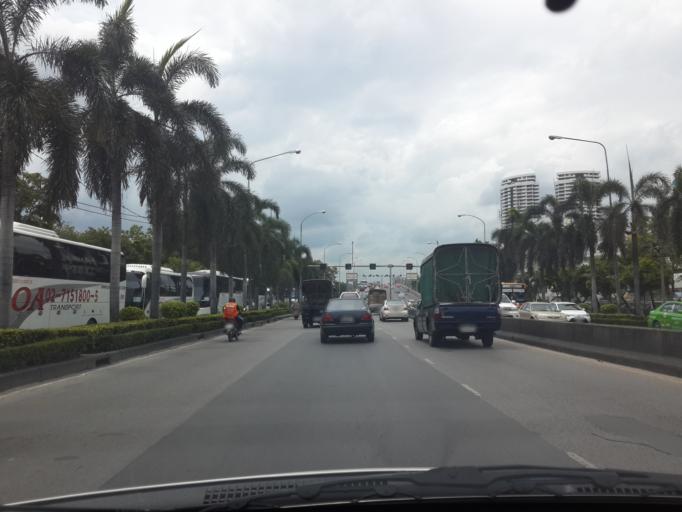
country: TH
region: Bangkok
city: Phra Nakhon
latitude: 13.7589
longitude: 100.4934
